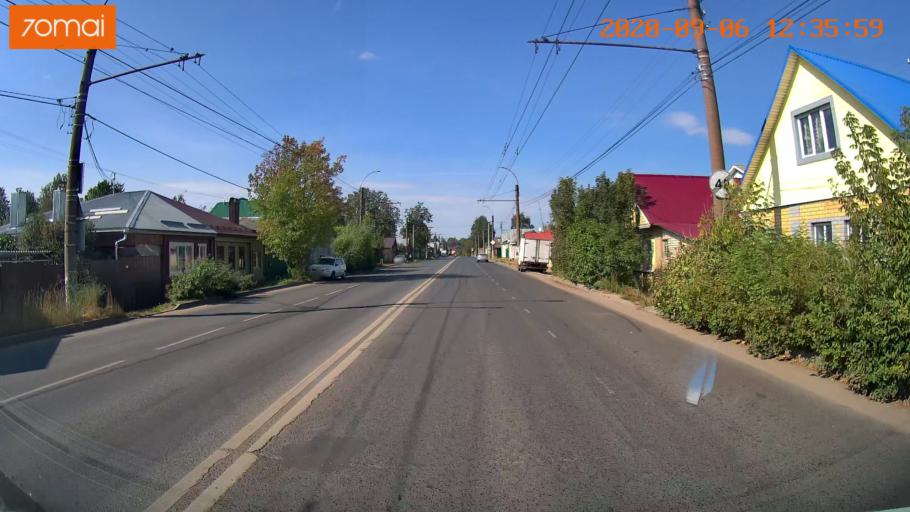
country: RU
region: Ivanovo
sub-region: Gorod Ivanovo
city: Ivanovo
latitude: 57.0212
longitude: 40.9895
